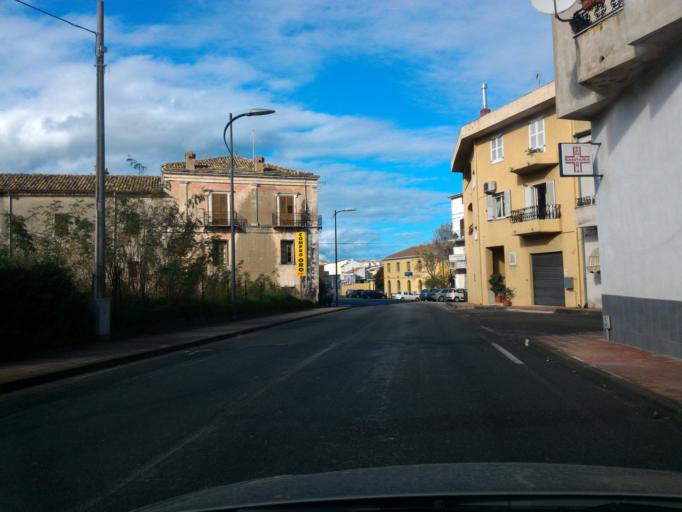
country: IT
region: Calabria
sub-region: Provincia di Crotone
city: Torretta
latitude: 39.4487
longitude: 17.0408
